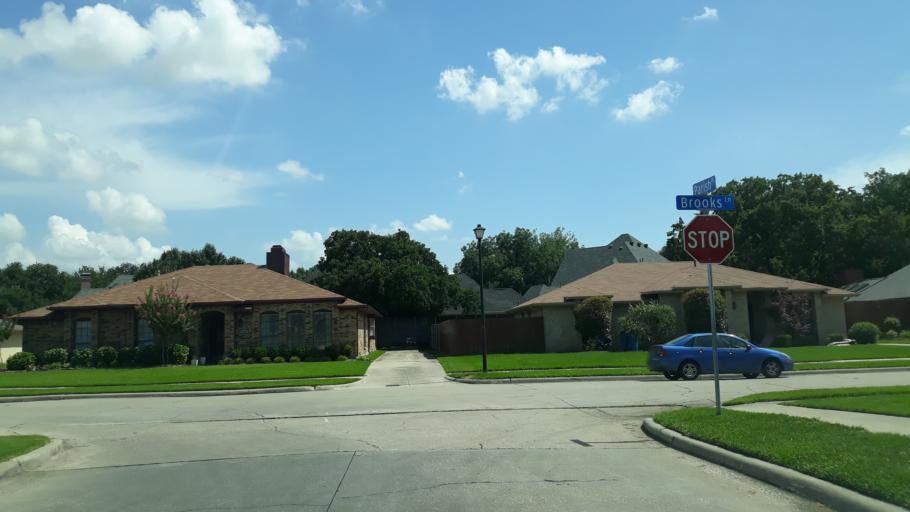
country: US
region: Texas
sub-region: Dallas County
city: Coppell
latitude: 32.9581
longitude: -97.0000
